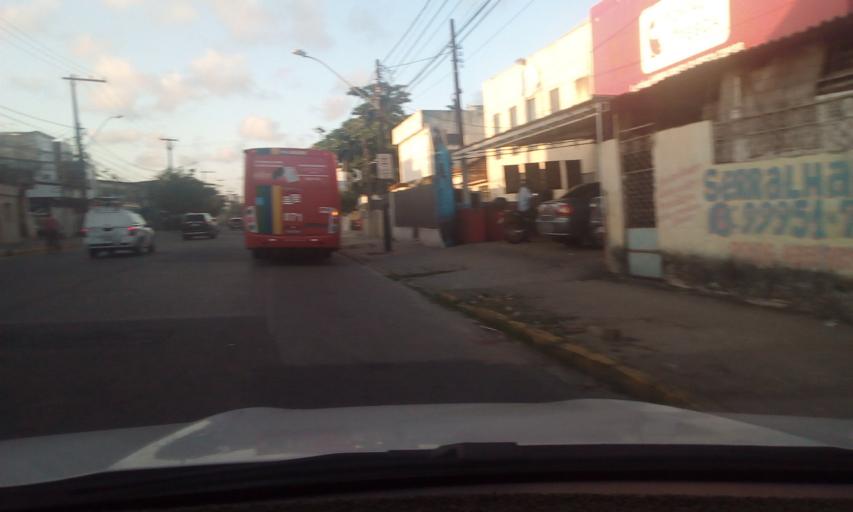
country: BR
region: Pernambuco
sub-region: Recife
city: Recife
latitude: -8.0755
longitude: -34.9074
